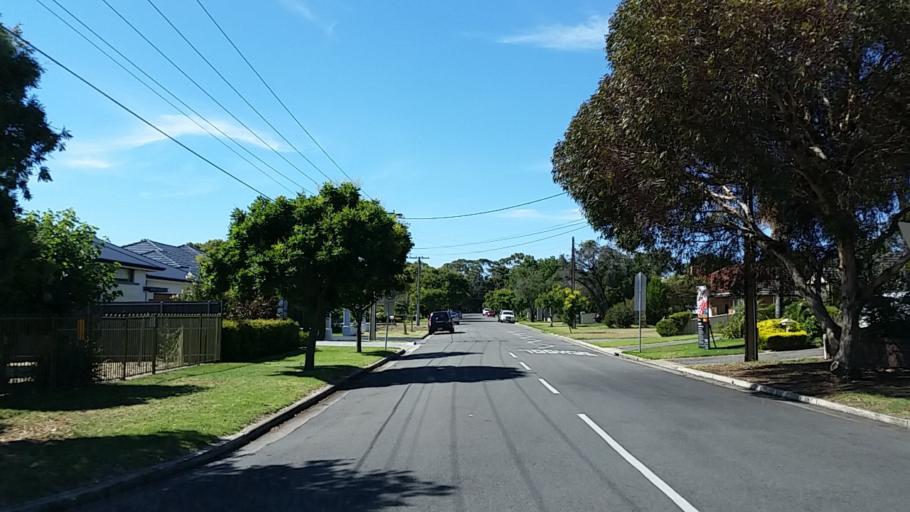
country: AU
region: South Australia
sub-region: Charles Sturt
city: Seaton
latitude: -34.9213
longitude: 138.5242
